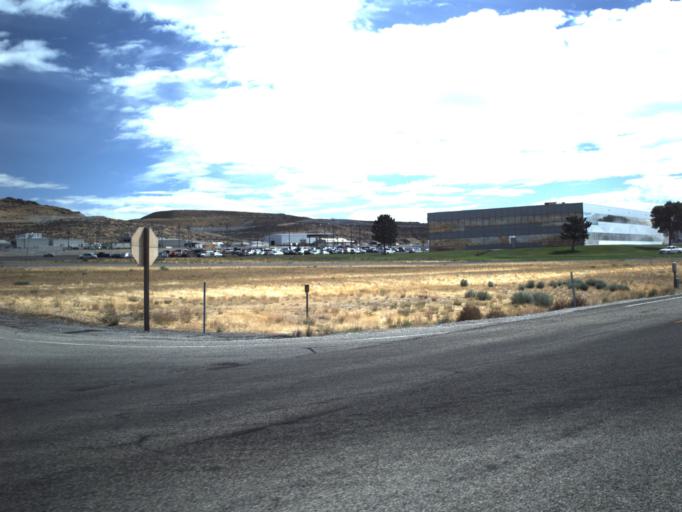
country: US
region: Utah
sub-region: Box Elder County
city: Tremonton
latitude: 41.6625
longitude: -112.4435
